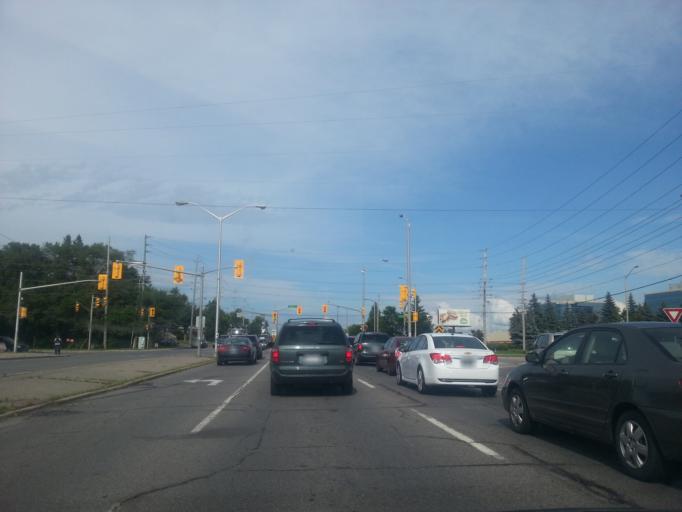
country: CA
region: Ontario
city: Ottawa
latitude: 45.4350
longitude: -75.6098
